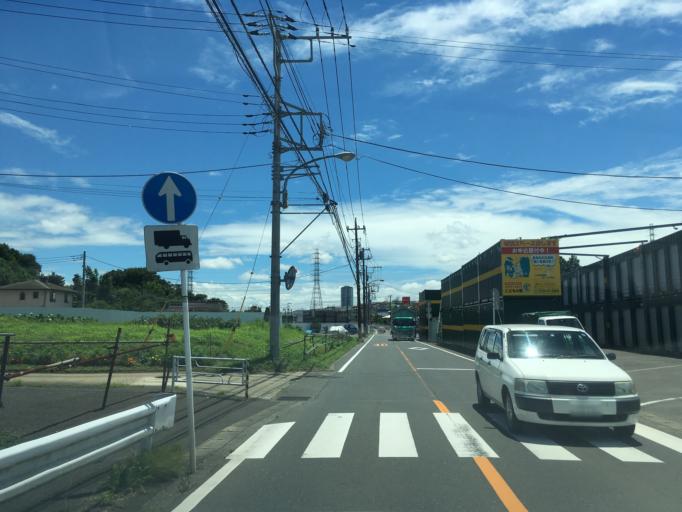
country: JP
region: Tokyo
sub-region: Machida-shi
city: Machida
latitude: 35.5489
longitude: 139.4909
